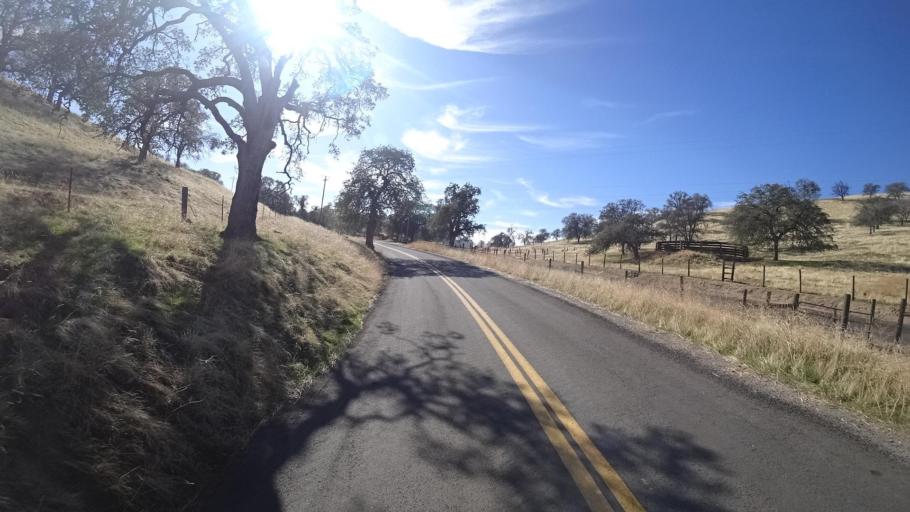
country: US
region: California
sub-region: Kern County
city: Oildale
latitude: 35.6510
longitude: -118.8406
